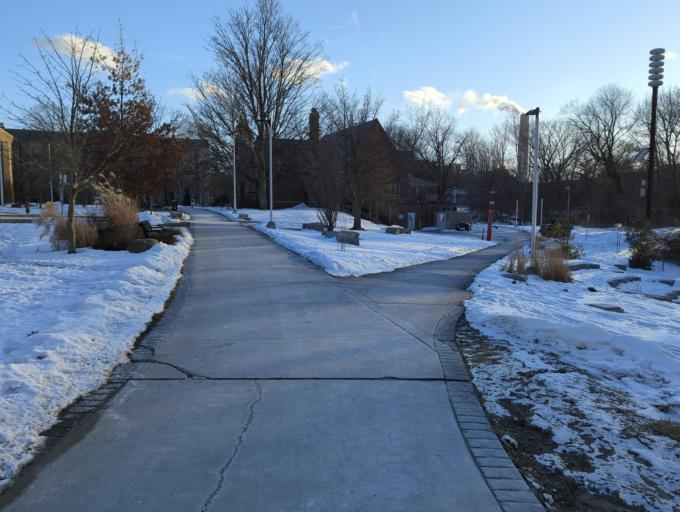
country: CA
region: Ontario
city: Hamilton
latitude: 43.2648
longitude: -79.9193
